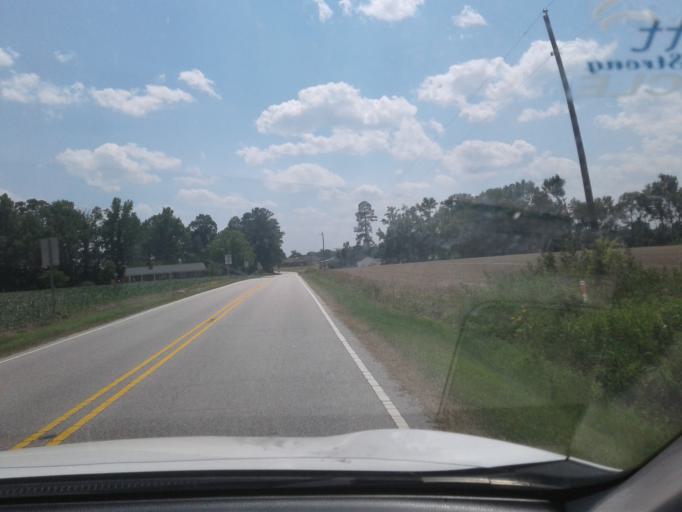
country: US
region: North Carolina
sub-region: Harnett County
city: Erwin
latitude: 35.2566
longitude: -78.6777
